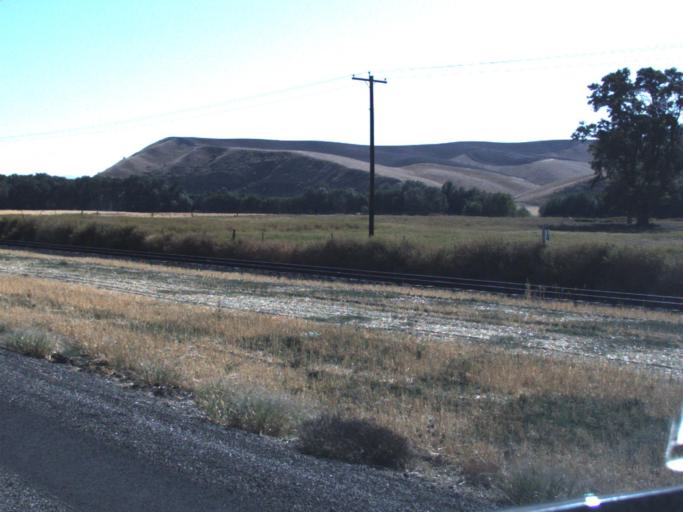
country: US
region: Washington
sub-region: Walla Walla County
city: Waitsburg
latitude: 46.2856
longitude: -118.2455
